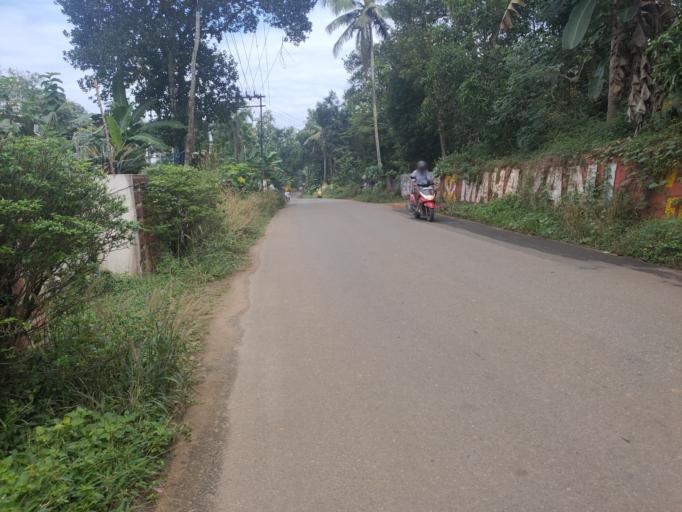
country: IN
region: Kerala
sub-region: Ernakulam
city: Muvattupula
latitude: 9.9865
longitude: 76.6372
